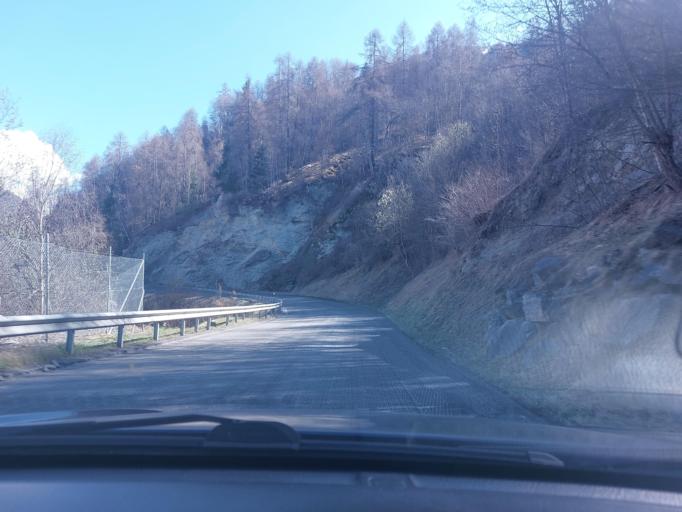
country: CH
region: Valais
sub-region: Herens District
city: Heremence
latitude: 46.1648
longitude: 7.4328
